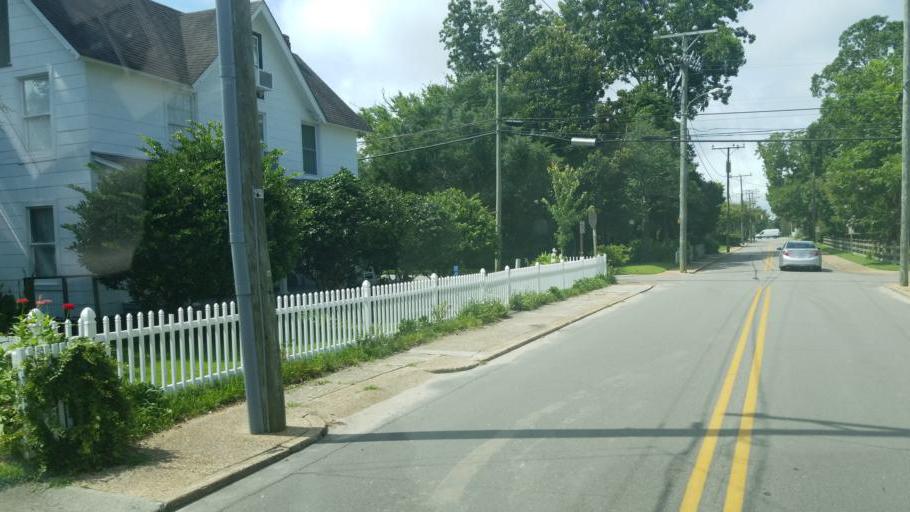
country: US
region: North Carolina
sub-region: Dare County
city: Manteo
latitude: 35.9077
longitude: -75.6729
